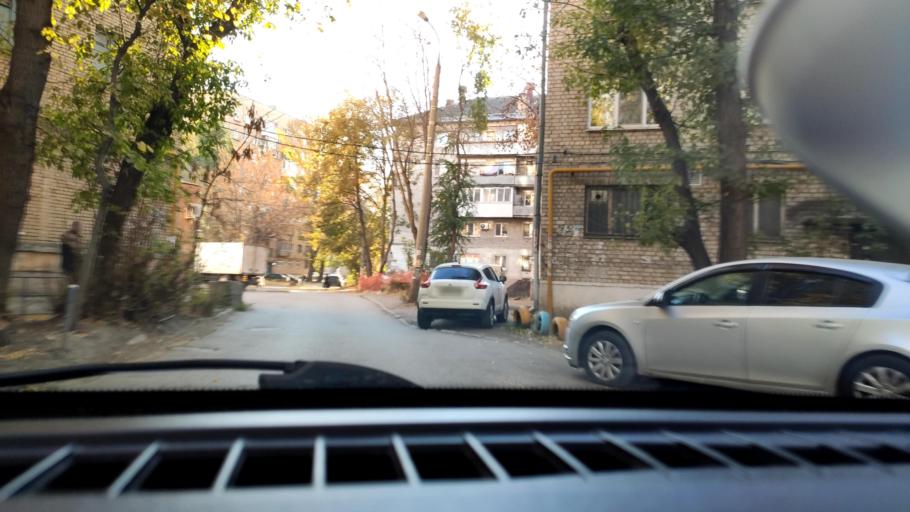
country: RU
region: Samara
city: Smyshlyayevka
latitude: 53.2198
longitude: 50.2734
